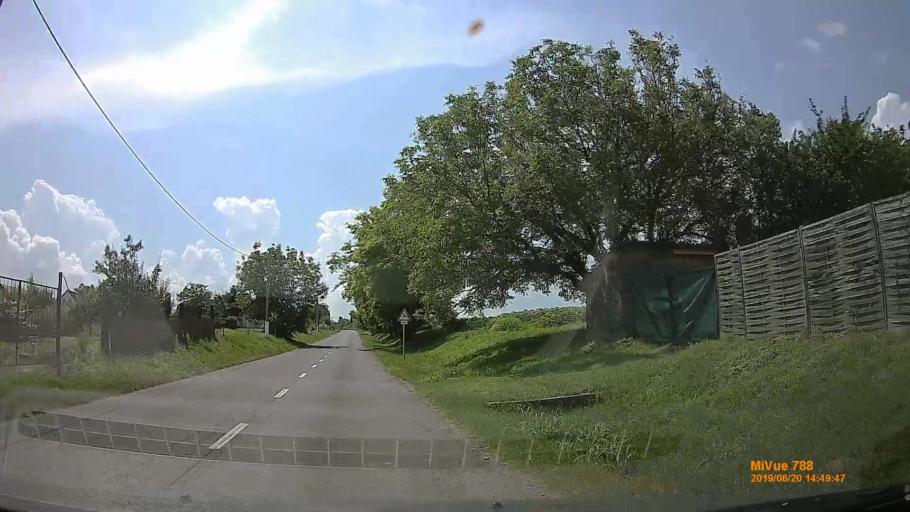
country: HU
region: Baranya
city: Kozarmisleny
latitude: 46.0152
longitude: 18.2724
